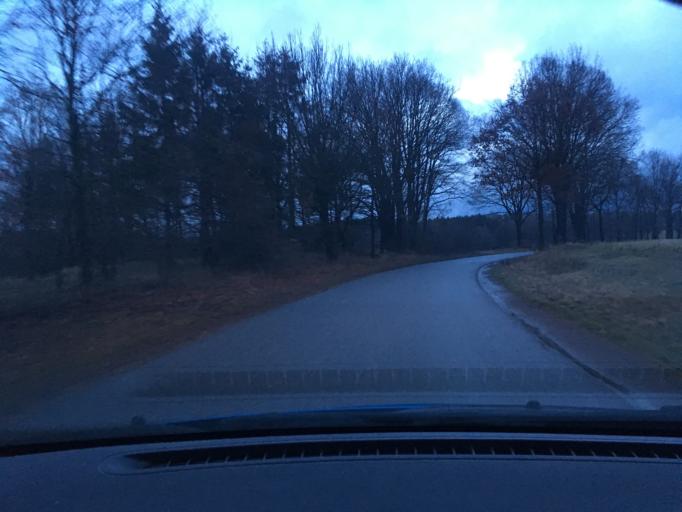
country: DE
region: Lower Saxony
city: Betzendorf
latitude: 53.1429
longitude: 10.3144
